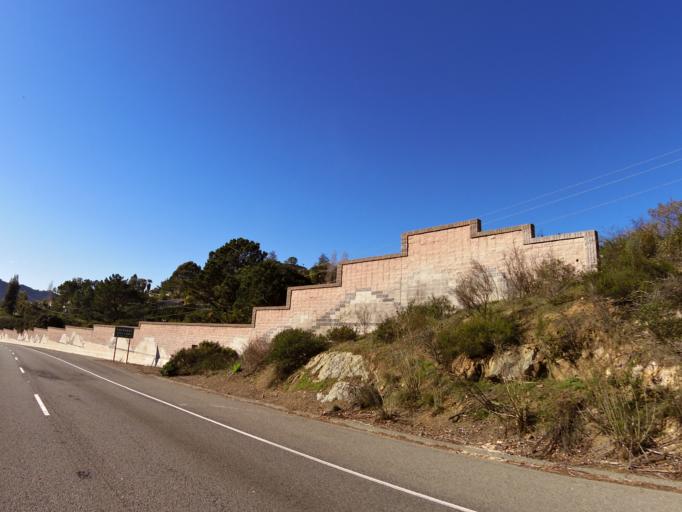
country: US
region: California
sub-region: Marin County
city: Larkspur
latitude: 37.9514
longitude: -122.5105
